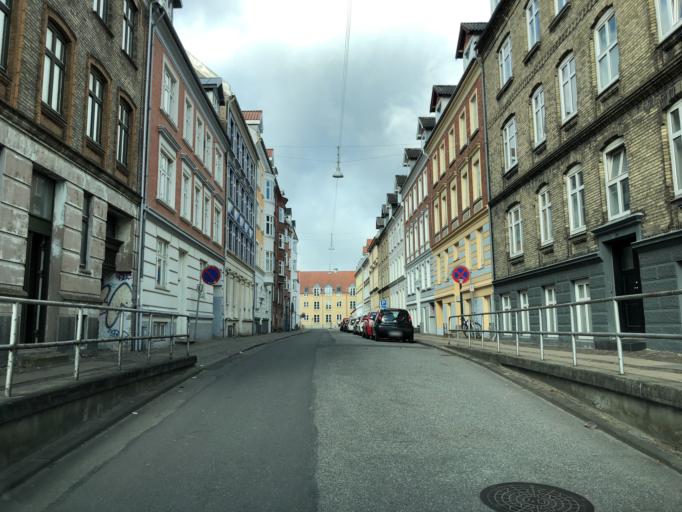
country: DK
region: North Denmark
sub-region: Alborg Kommune
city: Aalborg
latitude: 57.0507
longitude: 9.9095
